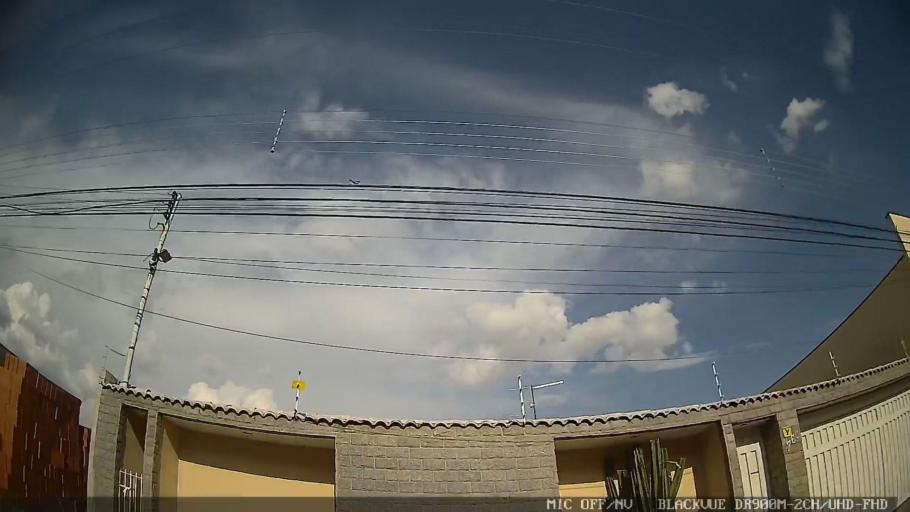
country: BR
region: Sao Paulo
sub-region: Braganca Paulista
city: Braganca Paulista
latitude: -22.9353
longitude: -46.5363
